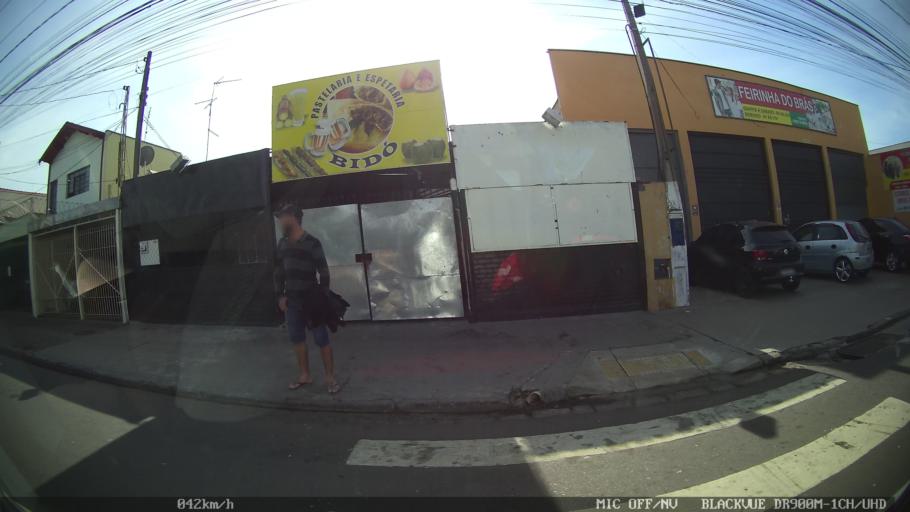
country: BR
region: Sao Paulo
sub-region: Piracicaba
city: Piracicaba
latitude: -22.7493
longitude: -47.6554
